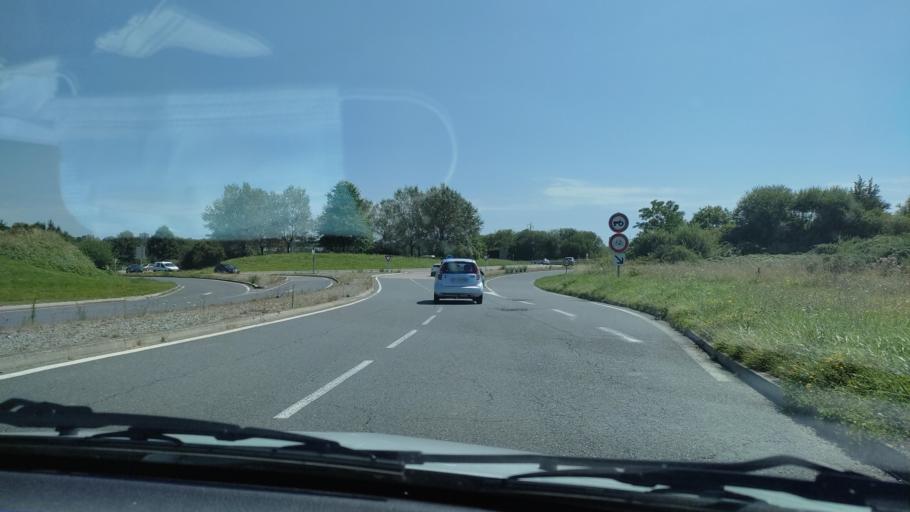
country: FR
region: Limousin
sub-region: Departement de la Haute-Vienne
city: Chaptelat
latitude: 45.8921
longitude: 1.2801
